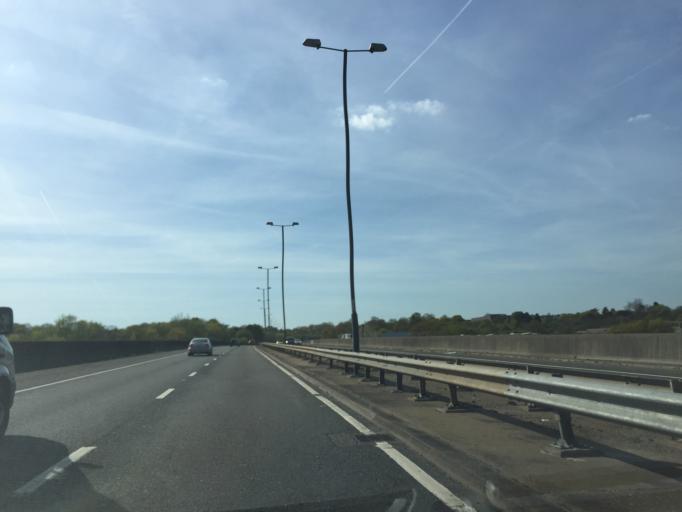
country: GB
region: England
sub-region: Greater London
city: Sidcup
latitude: 51.4127
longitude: 0.1147
